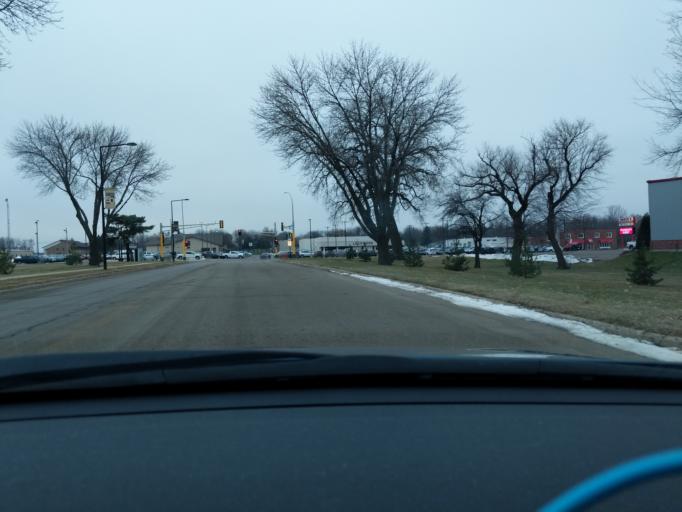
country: US
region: Minnesota
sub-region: Lyon County
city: Marshall
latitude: 44.4514
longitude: -95.7662
